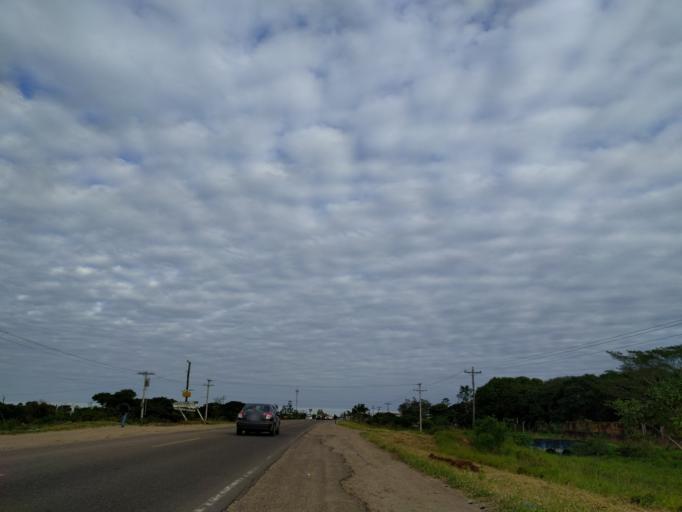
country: BO
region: Santa Cruz
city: Santa Rita
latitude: -17.8794
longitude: -63.2674
